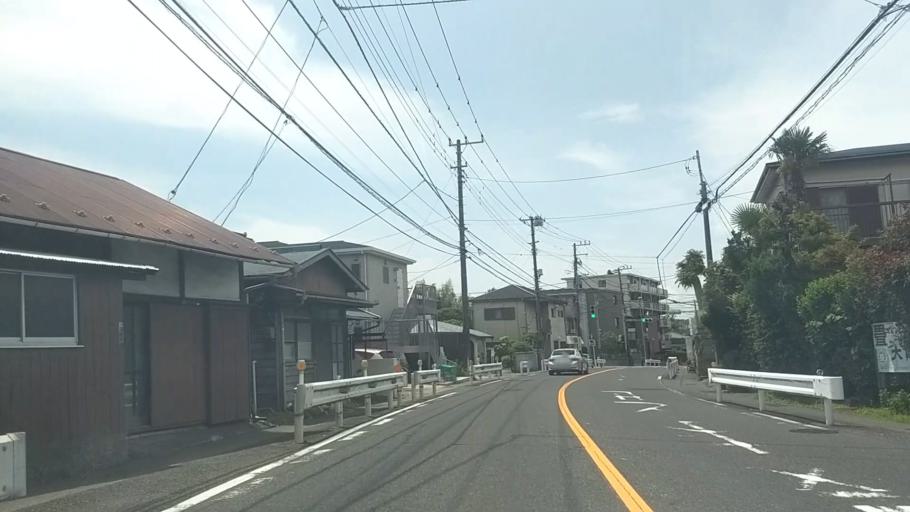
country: JP
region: Kanagawa
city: Fujisawa
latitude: 35.3463
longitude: 139.4916
